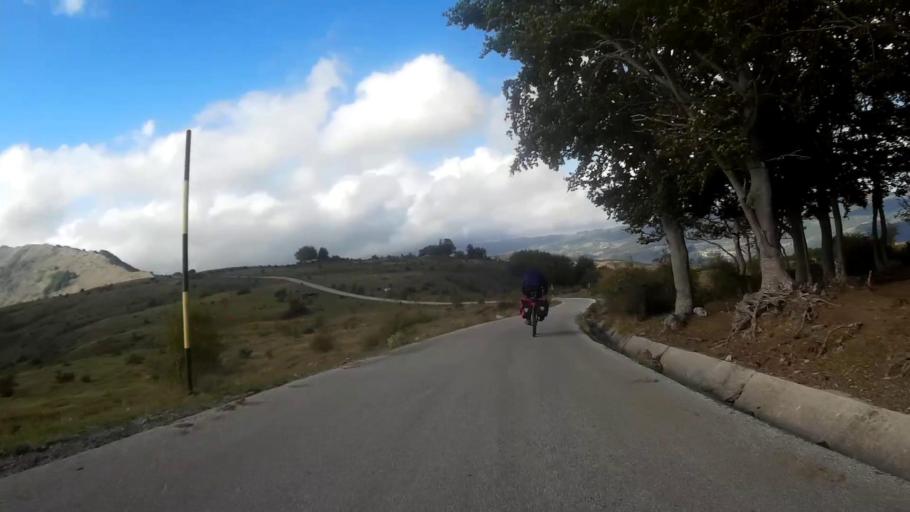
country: IT
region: Basilicate
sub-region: Provincia di Potenza
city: Viggianello
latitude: 39.9487
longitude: 16.1452
